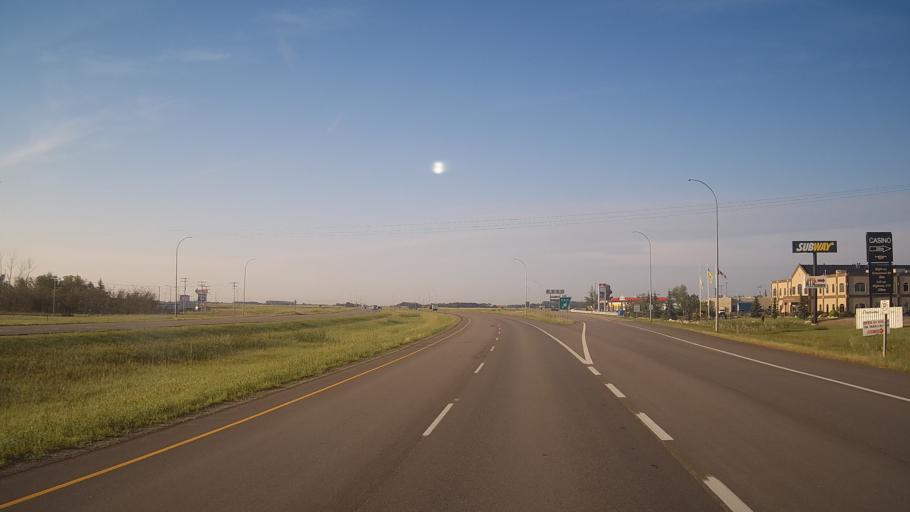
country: CA
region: Saskatchewan
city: Saskatoon
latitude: 52.0596
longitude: -106.6007
